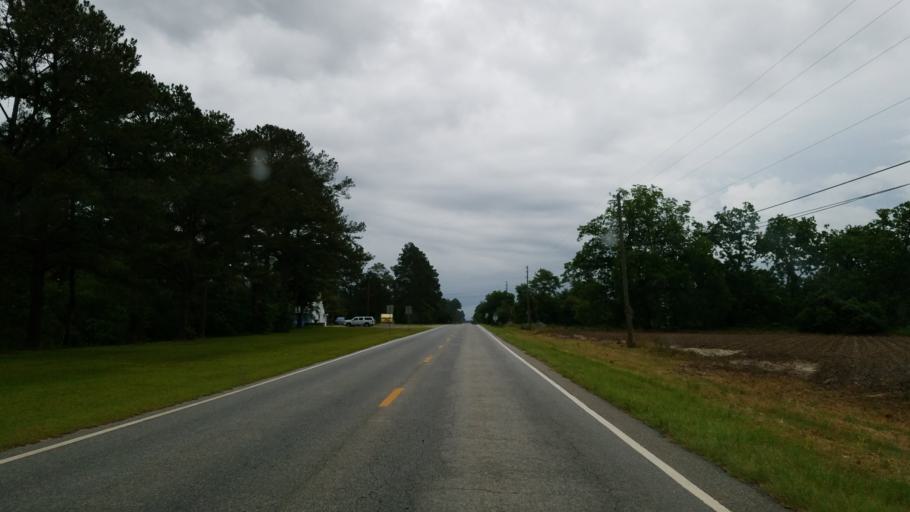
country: US
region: Georgia
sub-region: Berrien County
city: Ray City
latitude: 31.0662
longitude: -83.1689
